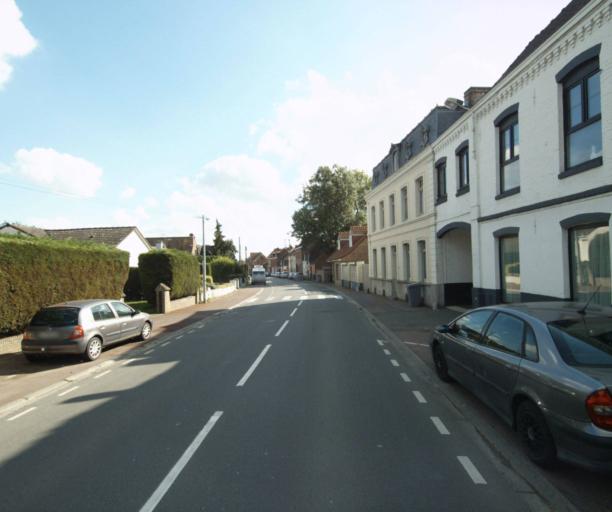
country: FR
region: Nord-Pas-de-Calais
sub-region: Departement du Nord
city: Sainghin-en-Weppes
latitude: 50.5682
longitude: 2.8925
